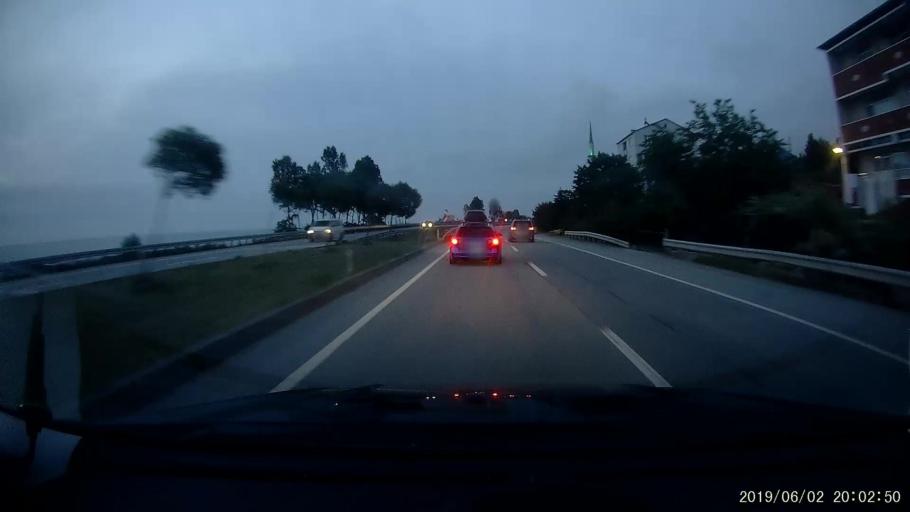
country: TR
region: Giresun
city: Tirebolu
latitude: 41.0148
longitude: 38.8816
